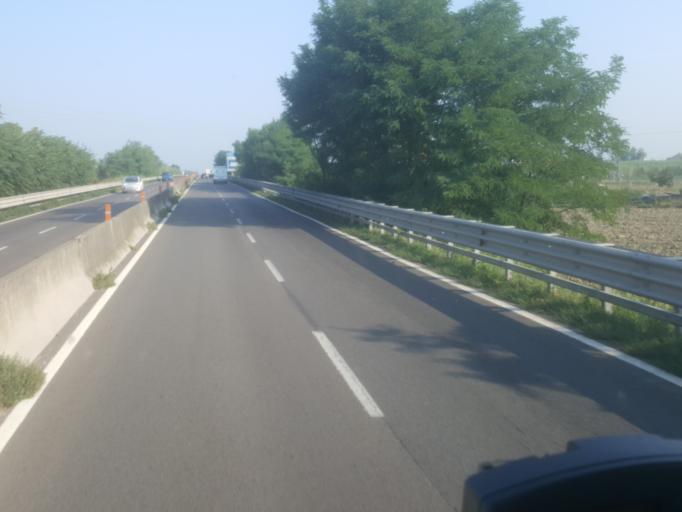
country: IT
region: Emilia-Romagna
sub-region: Provincia di Ravenna
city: Madonna Dell'Albero
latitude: 44.3904
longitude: 12.1870
